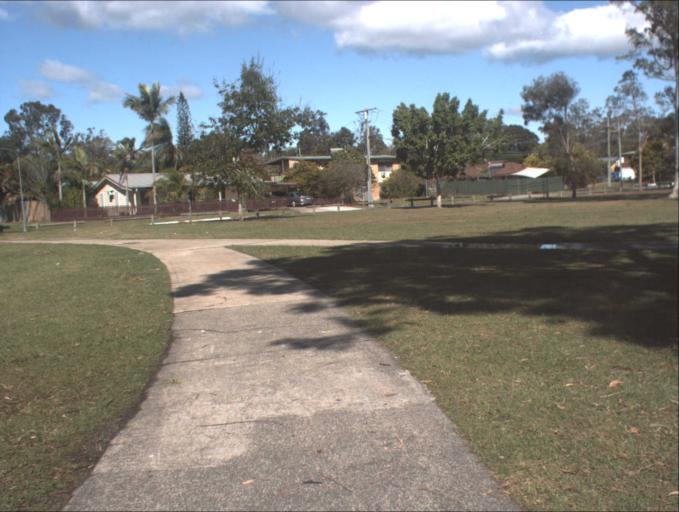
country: AU
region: Queensland
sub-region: Logan
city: Waterford West
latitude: -27.6770
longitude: 153.1080
